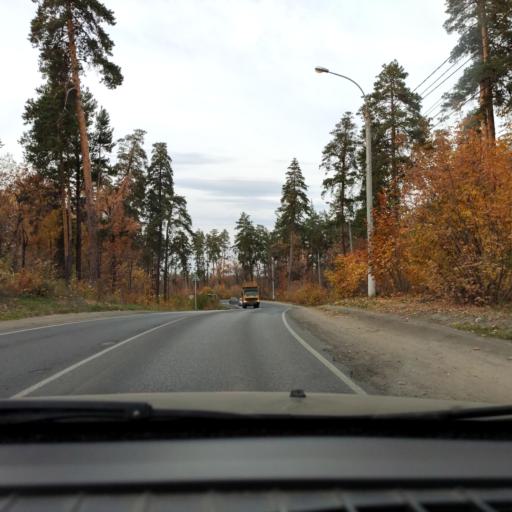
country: RU
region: Samara
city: Tol'yatti
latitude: 53.4896
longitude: 49.3069
